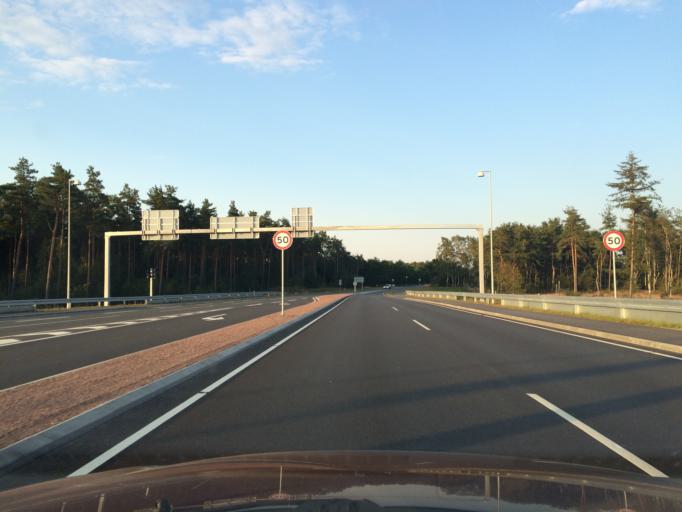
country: DK
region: Central Jutland
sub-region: Silkeborg Kommune
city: Svejbaek
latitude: 56.1700
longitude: 9.6042
